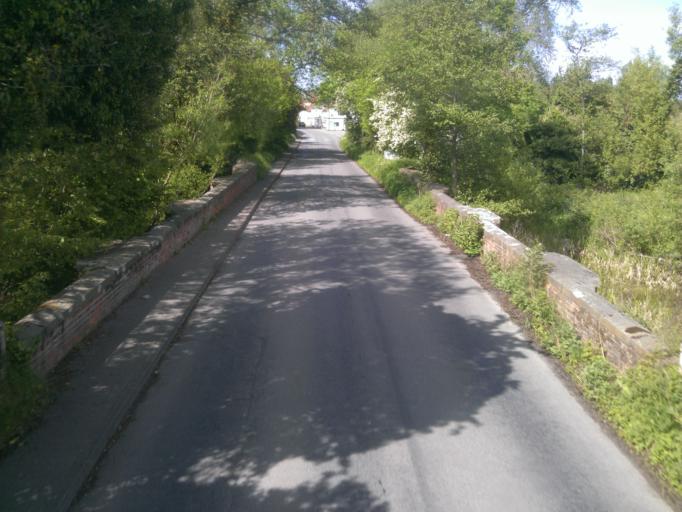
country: GB
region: England
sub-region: Suffolk
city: East Bergholt
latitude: 51.9638
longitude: 0.9716
